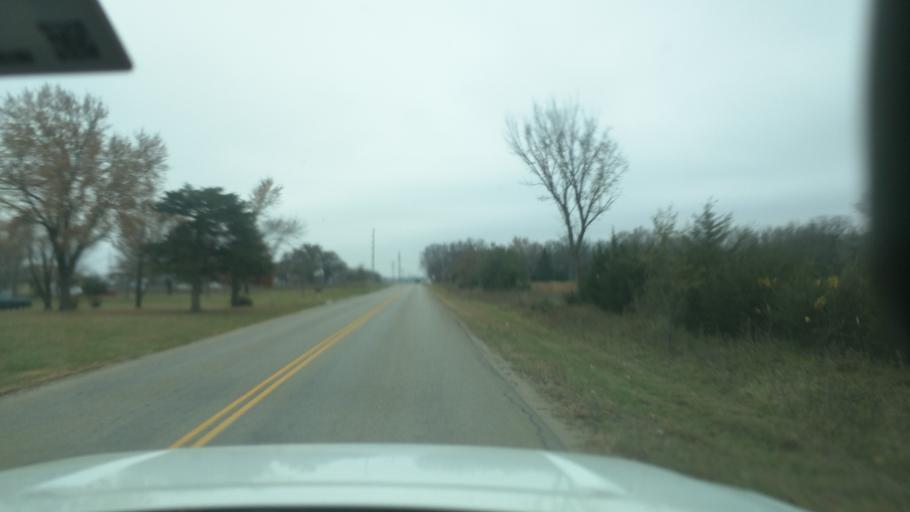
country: US
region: Kansas
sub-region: Lyon County
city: Emporia
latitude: 38.4945
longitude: -96.2528
